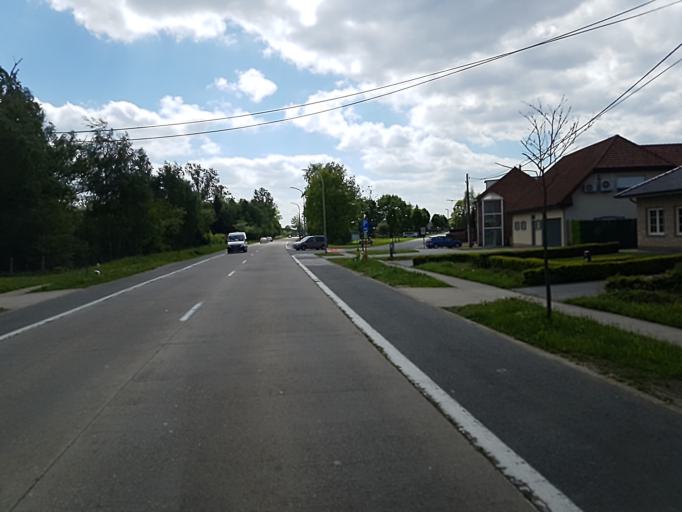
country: BE
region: Flanders
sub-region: Provincie Antwerpen
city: Westerlo
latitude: 51.0886
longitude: 4.9482
